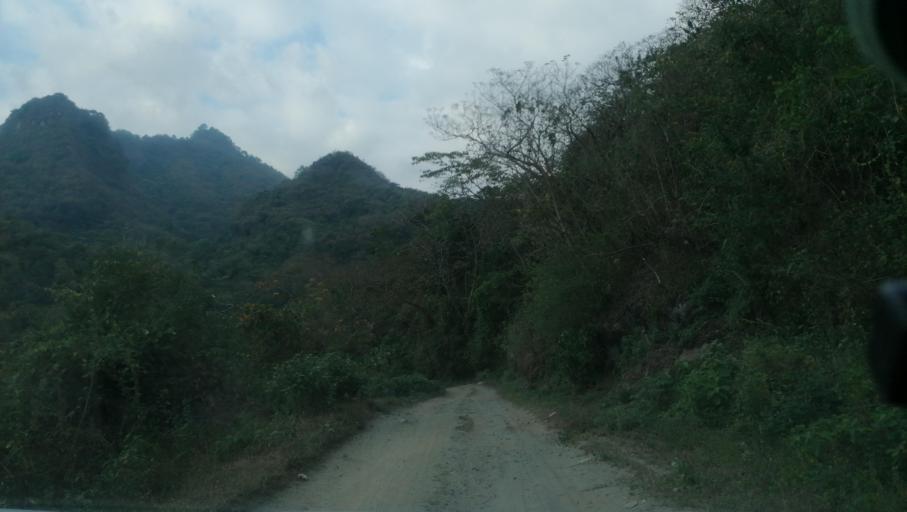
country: MX
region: Chiapas
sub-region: Cacahoatan
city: Benito Juarez
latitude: 15.1424
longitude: -92.1913
